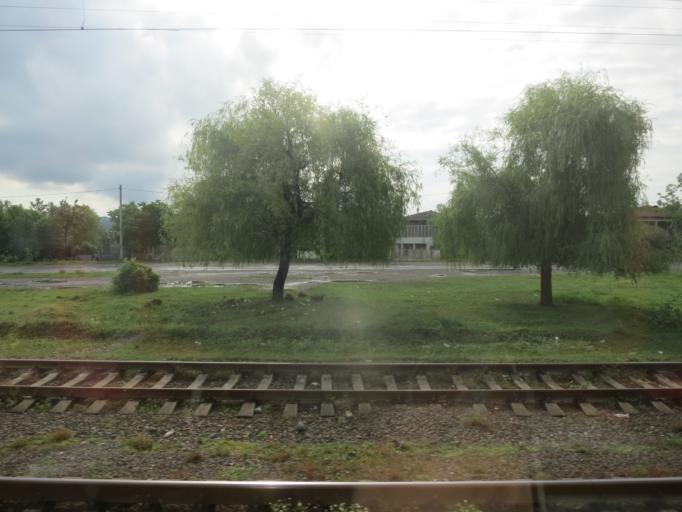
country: GE
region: Guria
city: Urek'i
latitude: 42.0430
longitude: 41.8139
